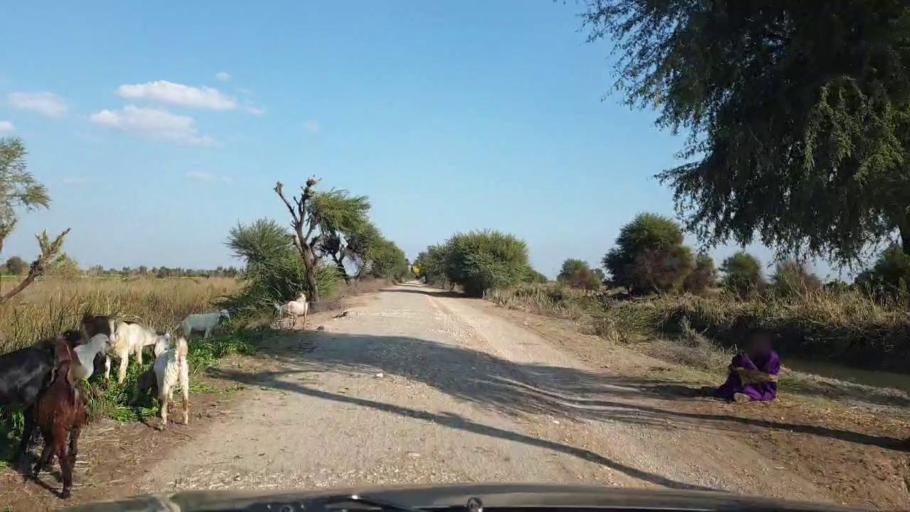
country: PK
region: Sindh
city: Sinjhoro
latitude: 25.9962
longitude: 68.7335
